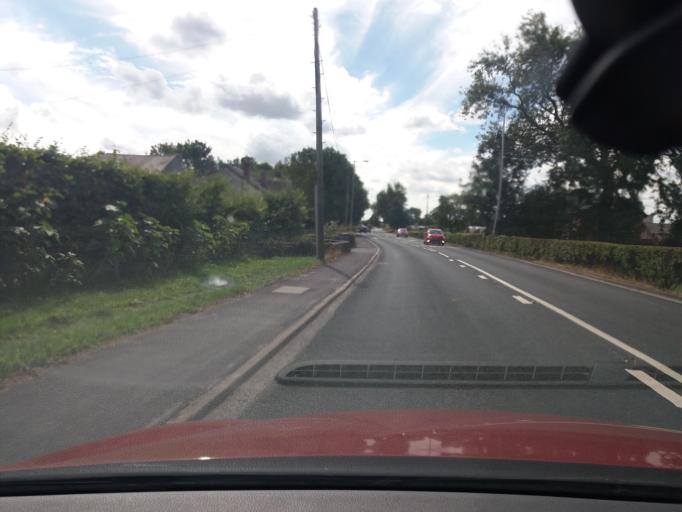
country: GB
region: England
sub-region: Lancashire
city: Coppull
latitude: 53.6318
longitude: -2.6854
